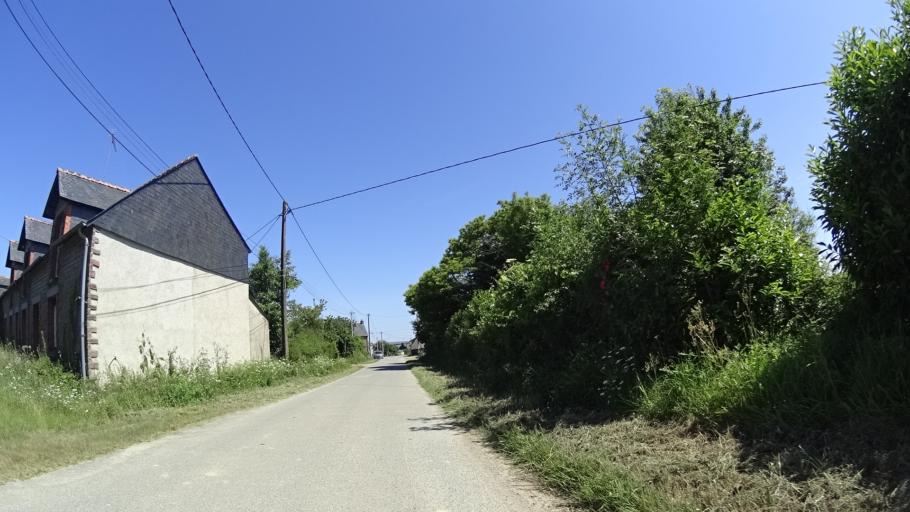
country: FR
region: Brittany
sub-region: Departement d'Ille-et-Vilaine
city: Messac
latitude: 47.7953
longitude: -1.8139
